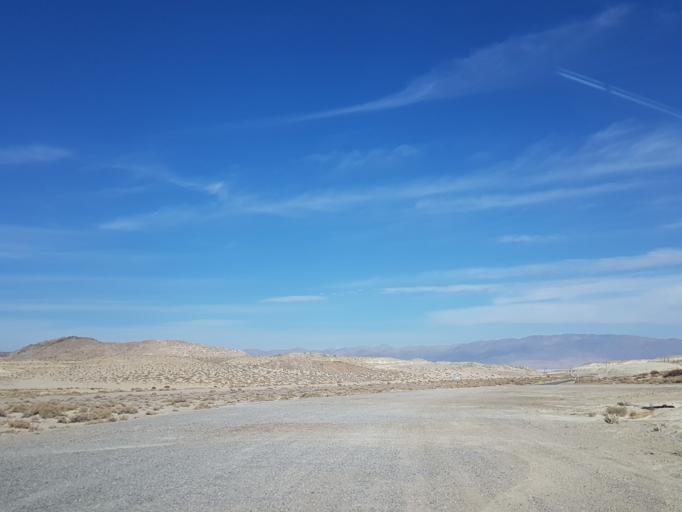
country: US
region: California
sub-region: San Bernardino County
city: Searles Valley
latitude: 35.6679
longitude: -117.4265
